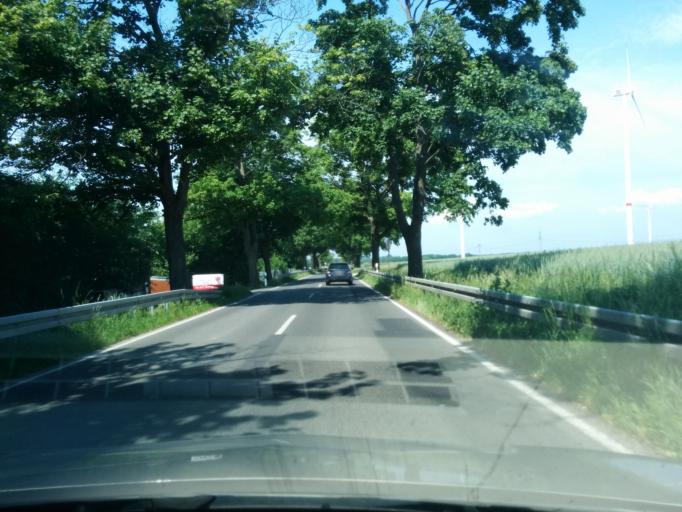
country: DE
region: Brandenburg
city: Ahrensfelde
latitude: 52.6134
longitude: 13.5921
